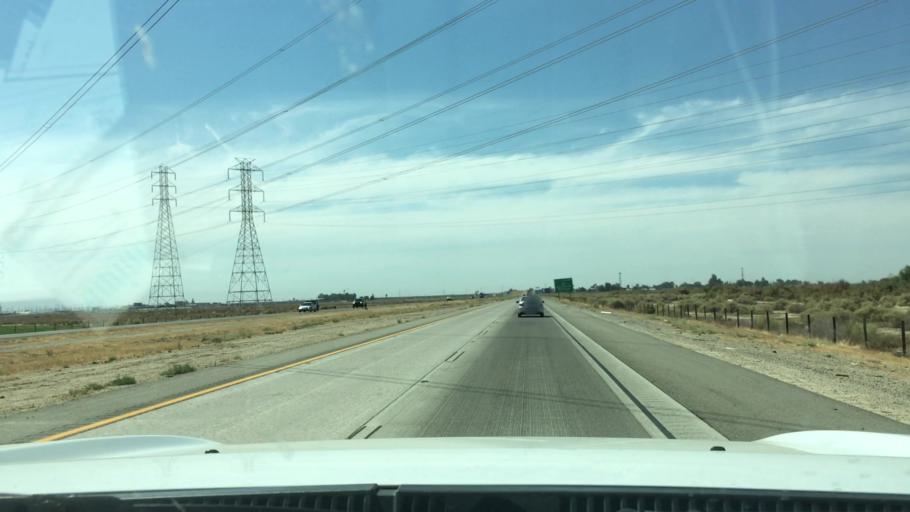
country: US
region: California
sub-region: Kern County
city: Buttonwillow
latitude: 35.3872
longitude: -119.3810
